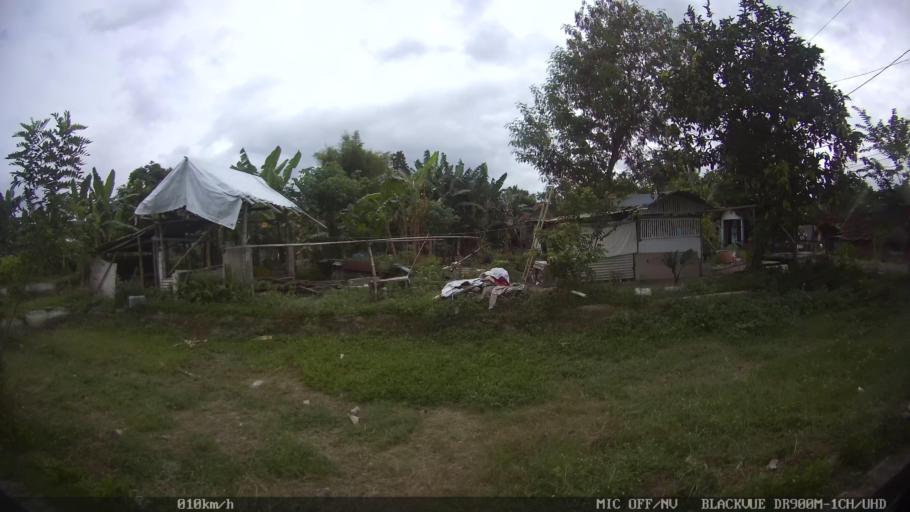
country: ID
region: Daerah Istimewa Yogyakarta
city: Depok
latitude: -7.8156
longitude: 110.4206
